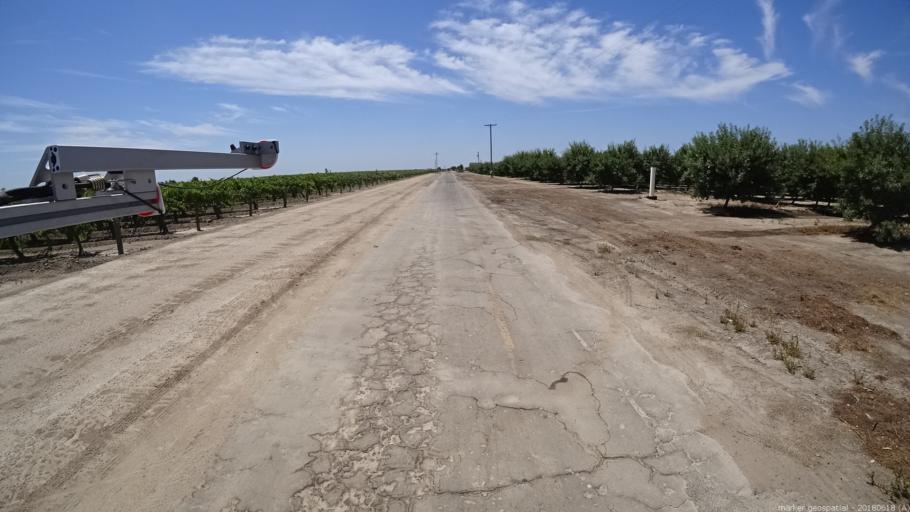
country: US
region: California
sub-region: Madera County
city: Parkwood
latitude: 36.8676
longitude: -120.1013
